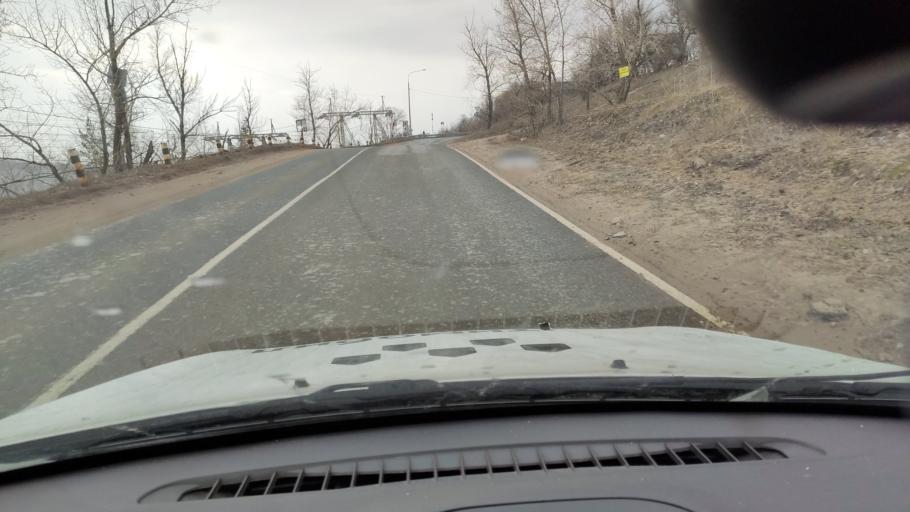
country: RU
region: Samara
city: Zhigulevsk
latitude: 53.4627
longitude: 49.5027
